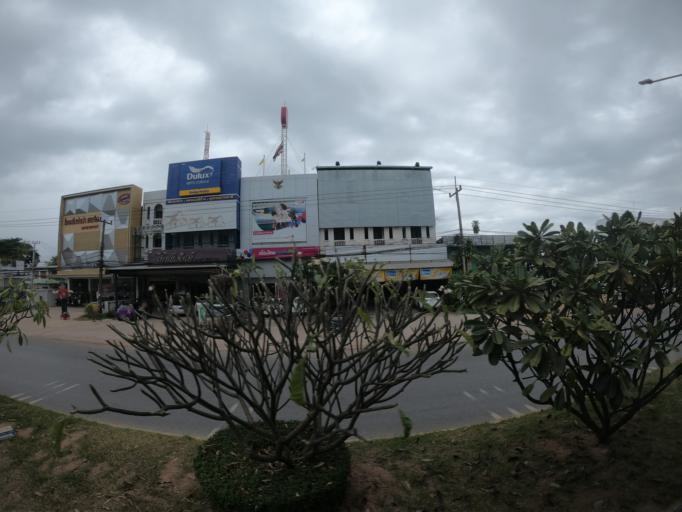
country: TH
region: Maha Sarakham
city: Maha Sarakham
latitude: 16.1766
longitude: 103.2965
